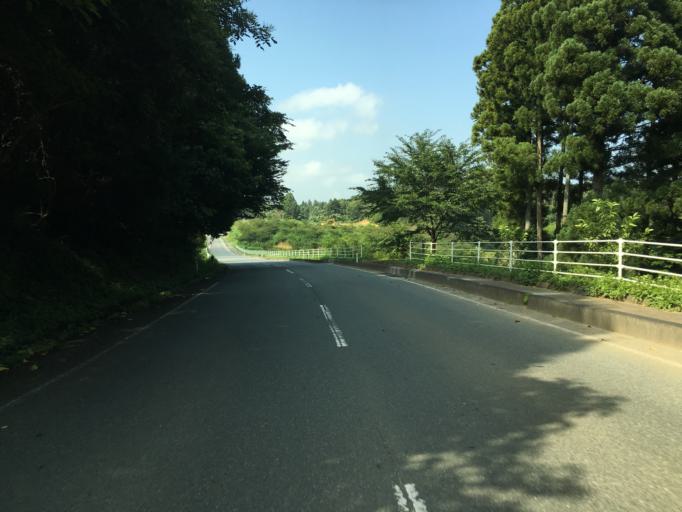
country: JP
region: Miyagi
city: Marumori
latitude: 37.8740
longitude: 140.8881
